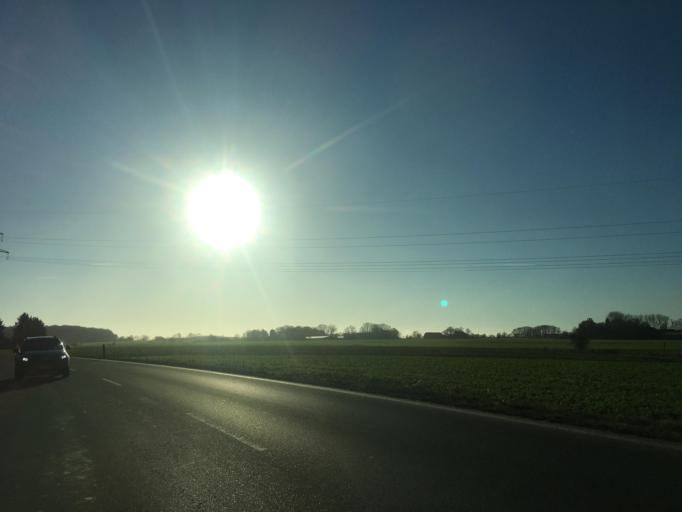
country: DE
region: North Rhine-Westphalia
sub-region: Regierungsbezirk Munster
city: Dulmen
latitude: 51.8707
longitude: 7.2864
